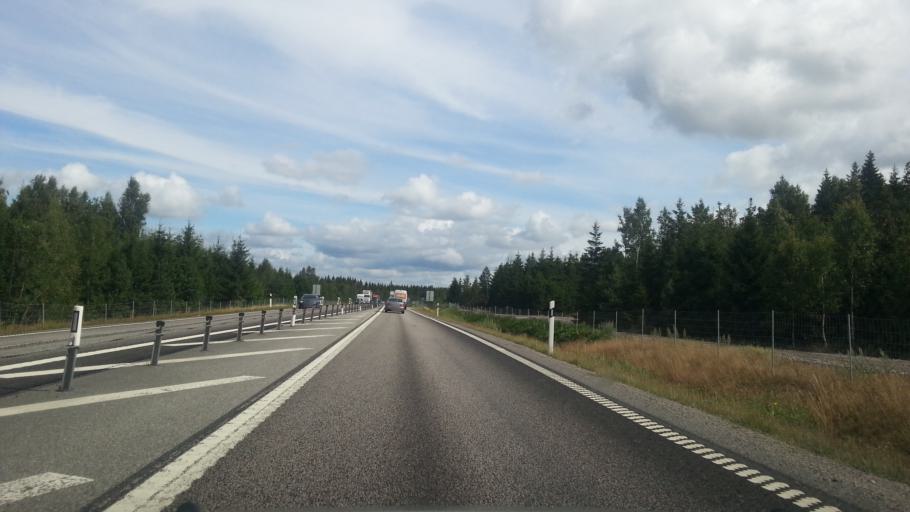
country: SE
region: Vaestra Goetaland
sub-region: Toreboda Kommun
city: Toereboda
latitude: 58.7924
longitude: 14.0208
